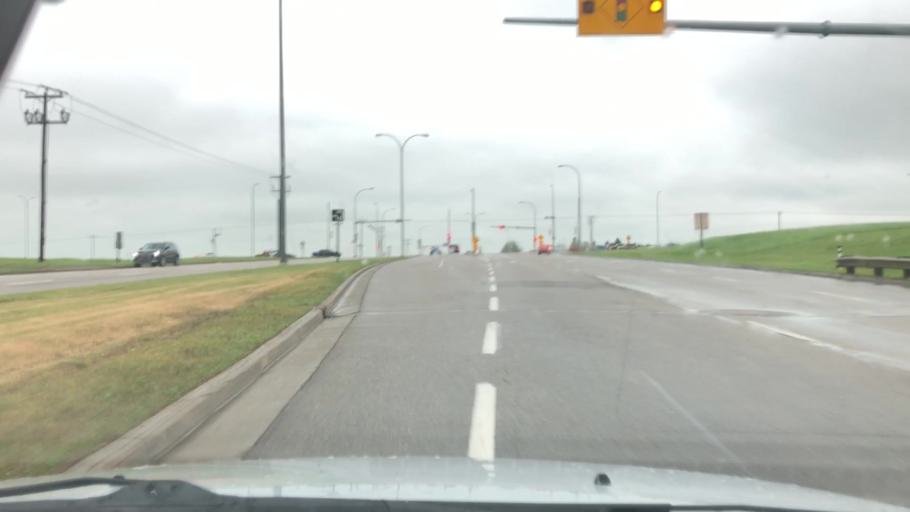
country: CA
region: Alberta
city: Sherwood Park
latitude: 53.5412
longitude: -113.2493
